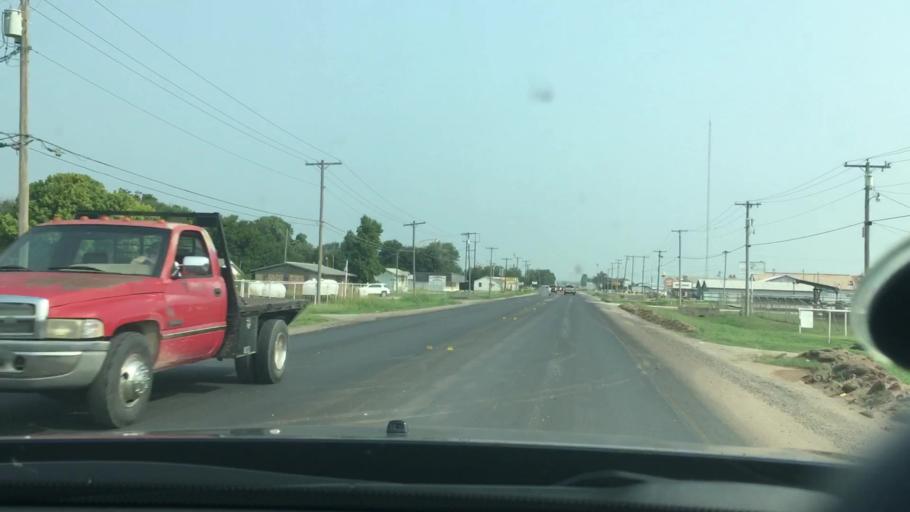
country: US
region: Oklahoma
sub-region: Garvin County
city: Lindsay
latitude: 34.8294
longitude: -97.5984
